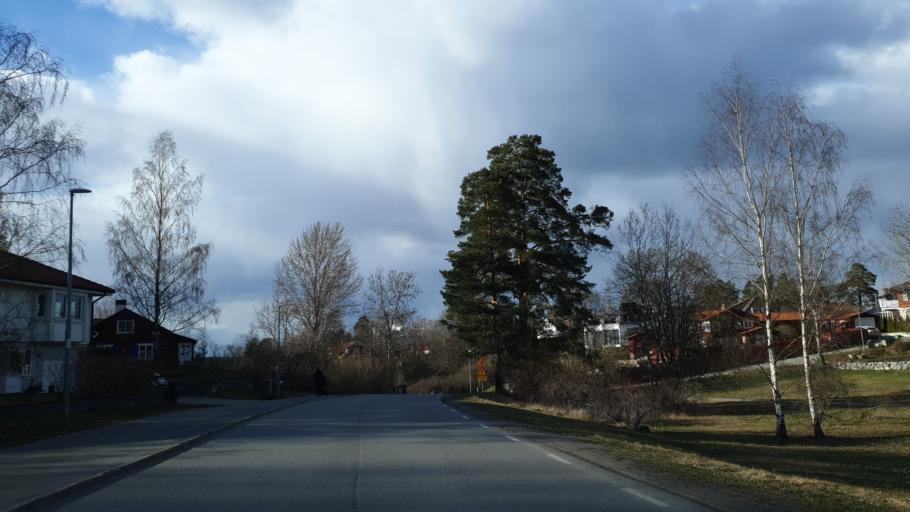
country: SE
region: Stockholm
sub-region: Lidingo
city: Lidingoe
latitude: 59.3882
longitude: 18.1196
